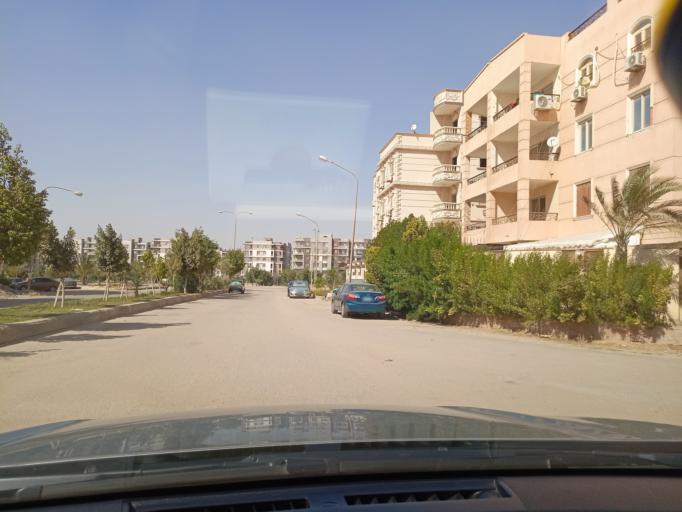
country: EG
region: Muhafazat al Qalyubiyah
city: Al Khankah
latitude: 30.2272
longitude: 31.4451
